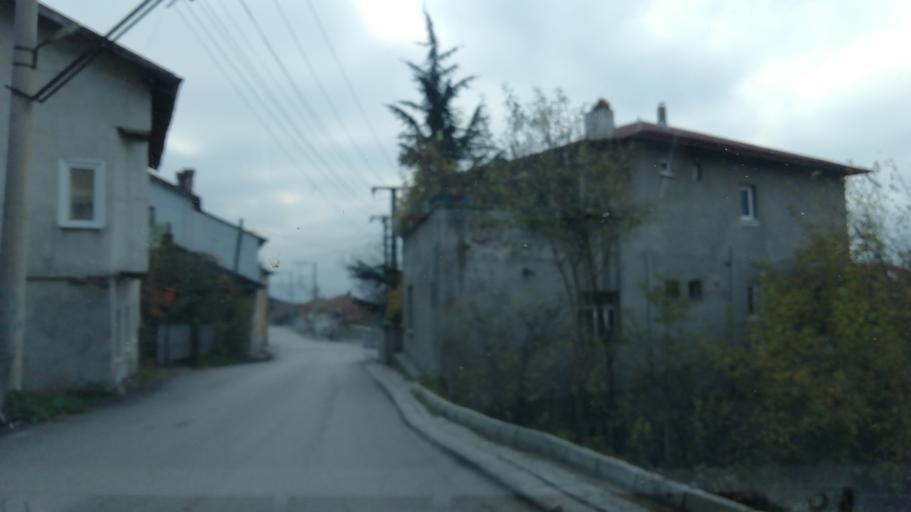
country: TR
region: Karabuk
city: Karabuk
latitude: 41.2153
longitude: 32.6286
